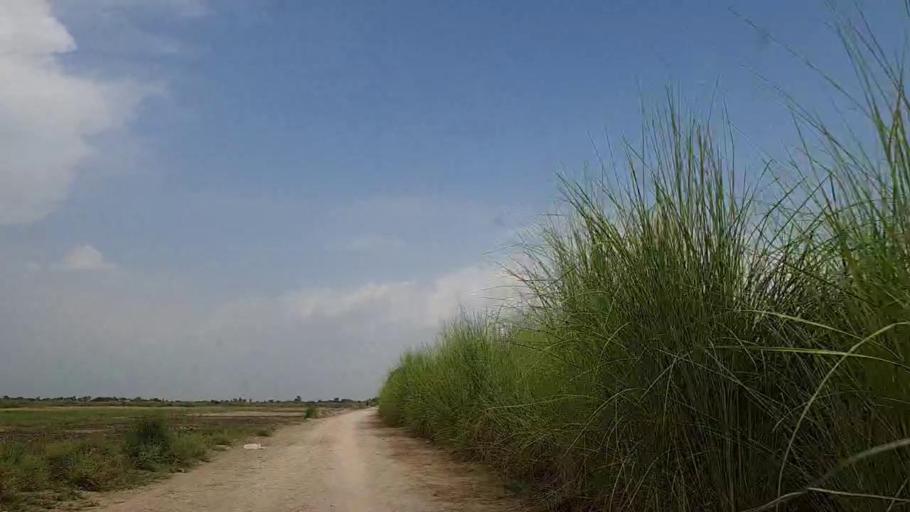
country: PK
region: Sindh
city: Khanpur
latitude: 27.8240
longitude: 69.5206
